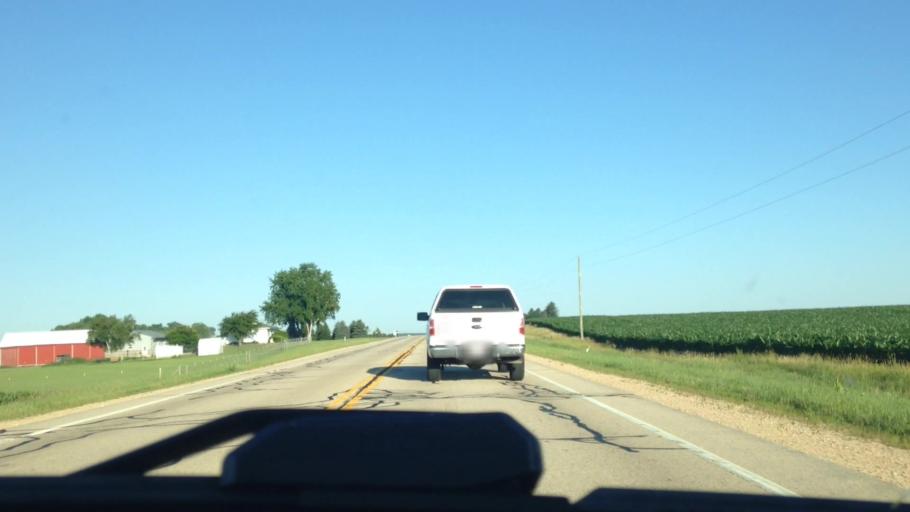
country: US
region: Wisconsin
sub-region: Columbia County
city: Rio
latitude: 43.3407
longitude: -89.1910
